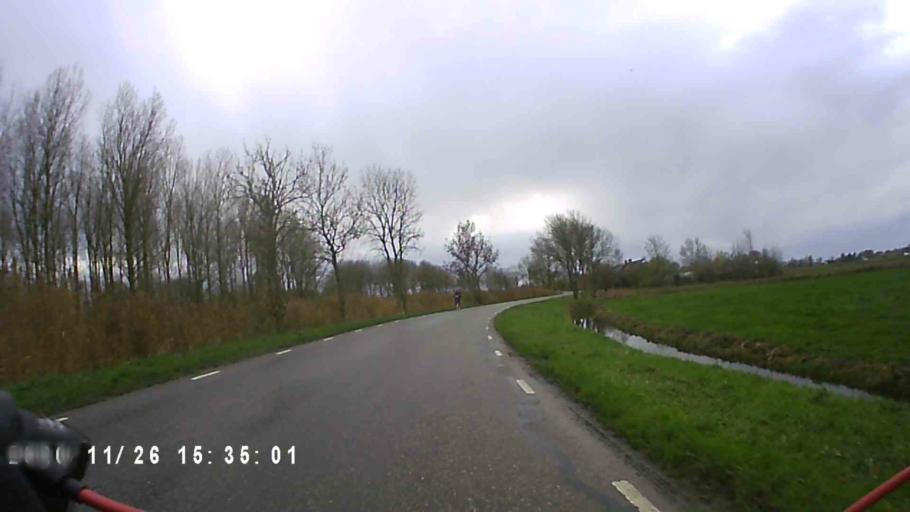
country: NL
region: Groningen
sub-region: Gemeente Slochteren
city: Slochteren
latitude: 53.3073
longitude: 6.7396
